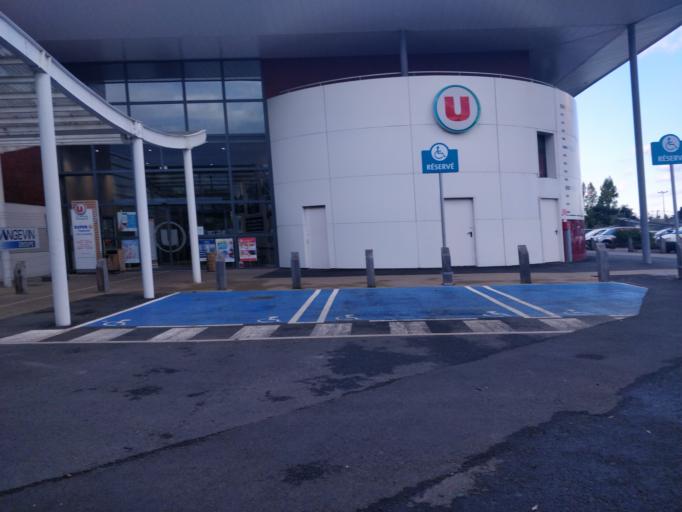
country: FR
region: Brittany
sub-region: Departement des Cotes-d'Armor
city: Tregastel
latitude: 48.8223
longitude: -3.4961
